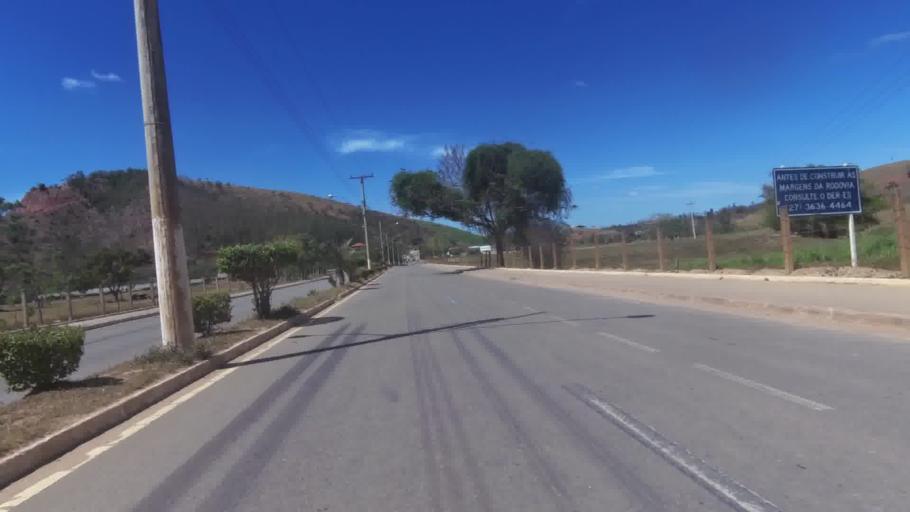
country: BR
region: Espirito Santo
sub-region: Cachoeiro De Itapemirim
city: Cachoeiro de Itapemirim
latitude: -20.9215
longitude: -41.1886
